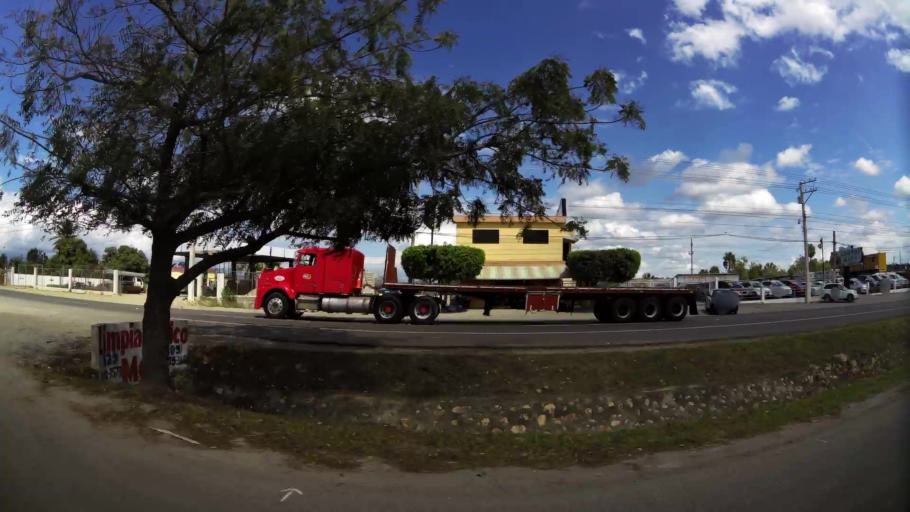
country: DO
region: La Vega
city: Rio Verde Arriba
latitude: 19.3664
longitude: -70.6031
